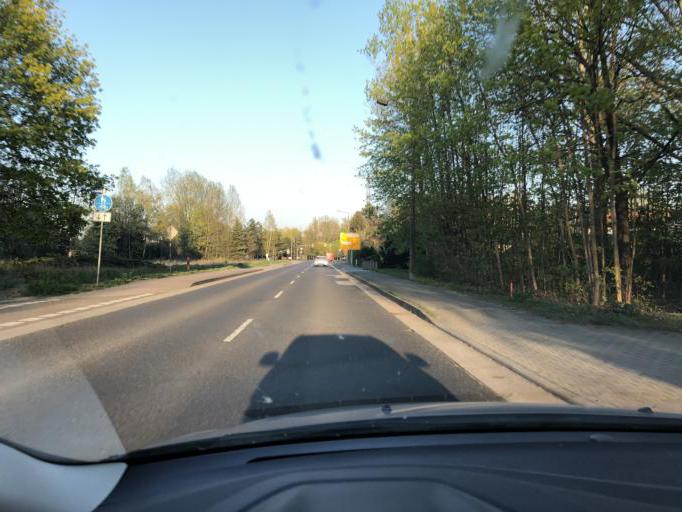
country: DE
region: Brandenburg
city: Spremberg
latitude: 51.5242
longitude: 14.3315
